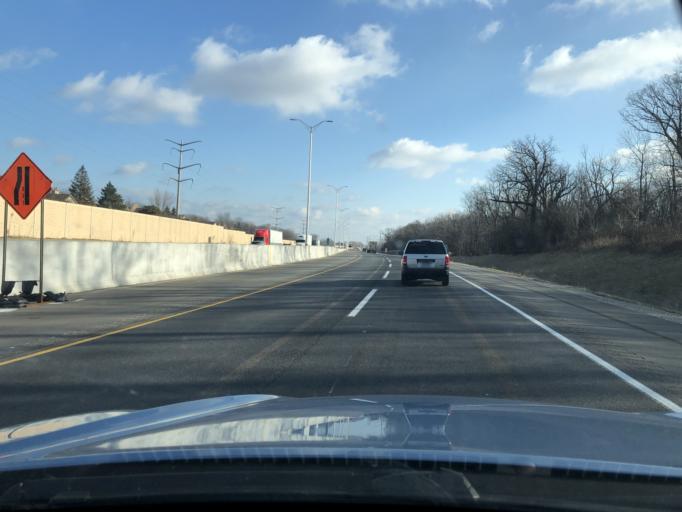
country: US
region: Illinois
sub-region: Cook County
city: Northbrook
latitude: 42.1443
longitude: -87.8272
